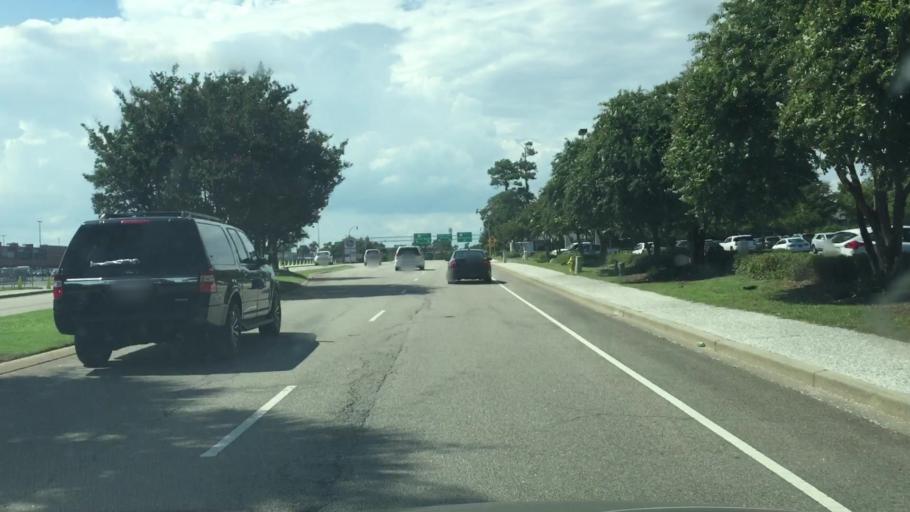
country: US
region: South Carolina
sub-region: Horry County
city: North Myrtle Beach
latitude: 33.8260
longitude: -78.6772
